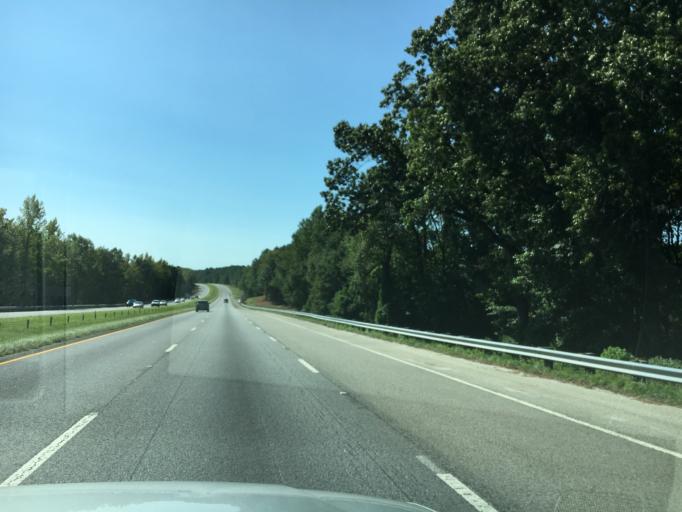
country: US
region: South Carolina
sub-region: Spartanburg County
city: Woodruff
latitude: 34.7451
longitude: -81.9547
